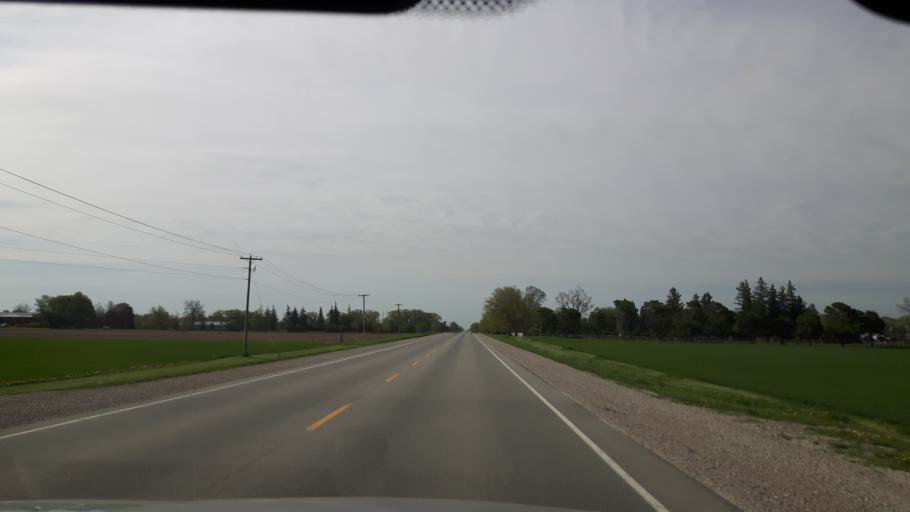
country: CA
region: Ontario
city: South Huron
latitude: 43.4248
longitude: -81.4967
